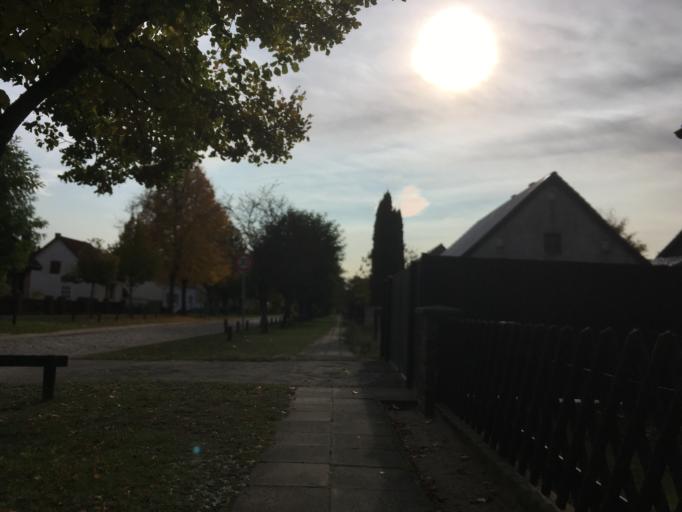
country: DE
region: Brandenburg
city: Templin
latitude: 52.9983
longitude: 13.4775
